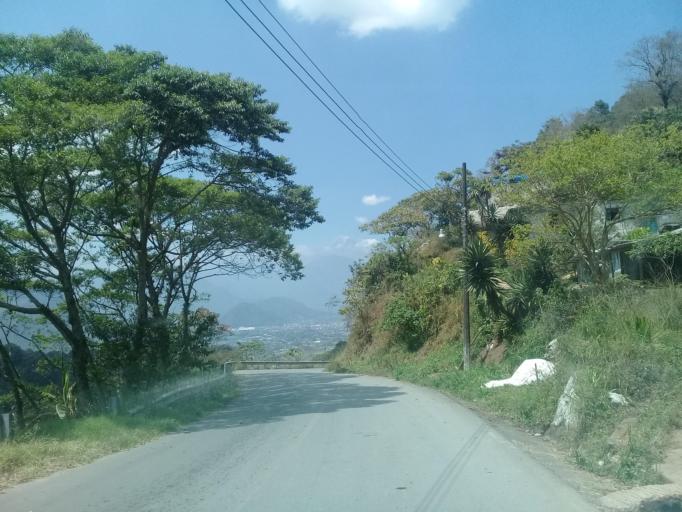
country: MX
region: Veracruz
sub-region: Tlilapan
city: Tonalixco
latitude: 18.7986
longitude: -97.0566
